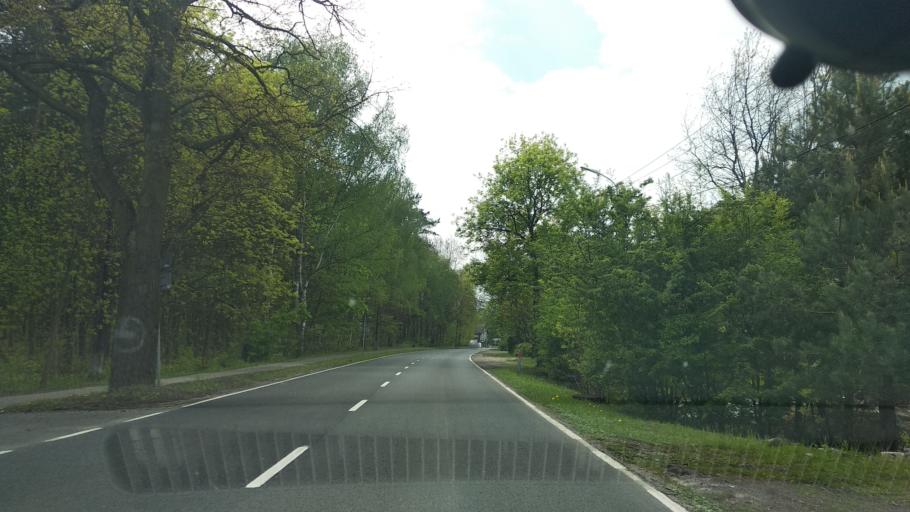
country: PL
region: Silesian Voivodeship
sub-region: Powiat mikolowski
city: Mikolow
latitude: 50.2286
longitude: 18.9316
